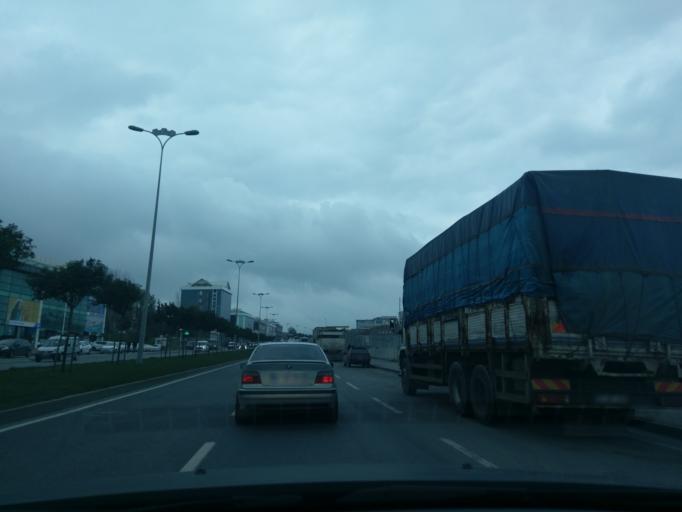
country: TR
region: Istanbul
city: Basaksehir
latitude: 41.0722
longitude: 28.8026
